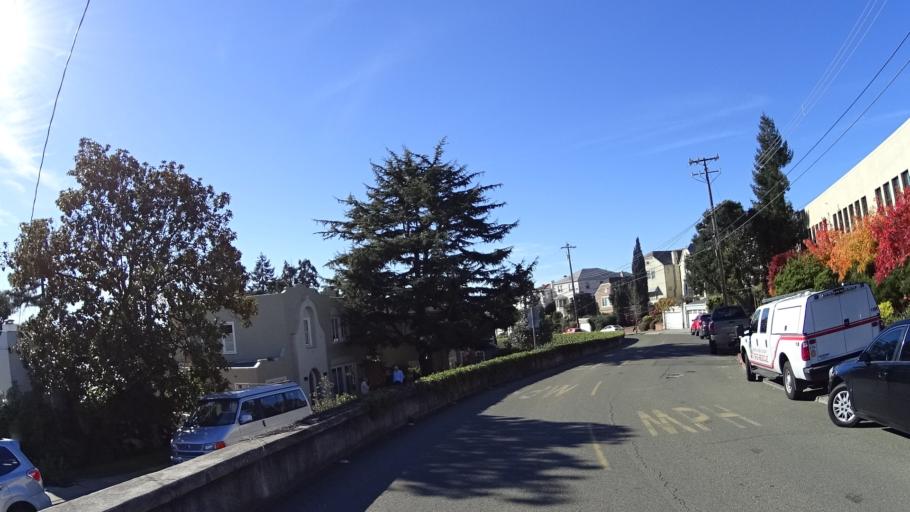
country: US
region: California
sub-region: Alameda County
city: Piedmont
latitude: 37.8194
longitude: -122.2353
